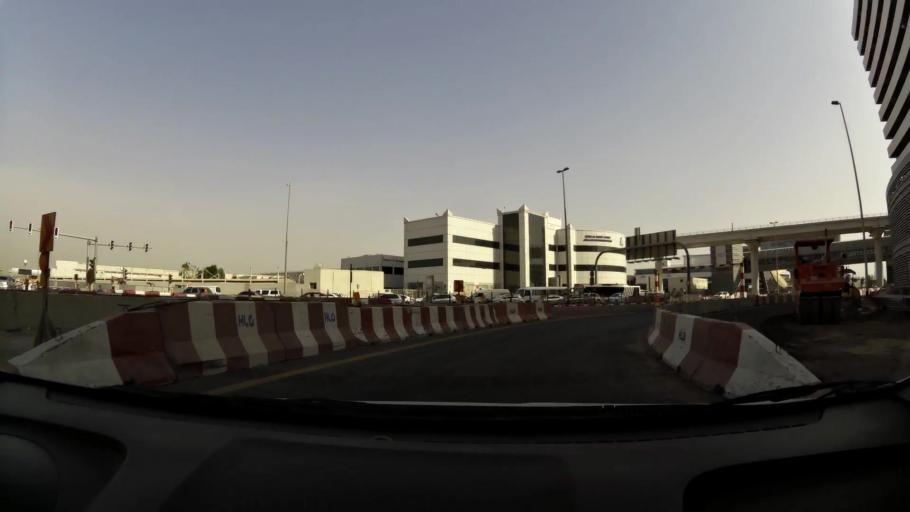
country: AE
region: Ash Shariqah
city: Sharjah
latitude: 25.2409
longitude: 55.3681
